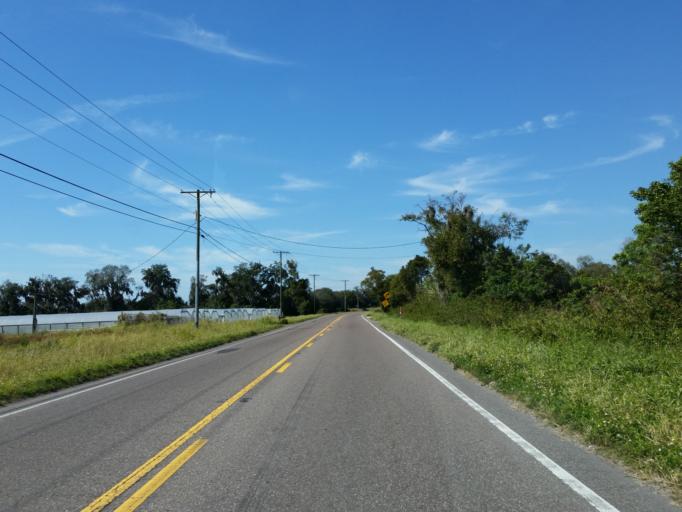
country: US
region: Florida
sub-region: Hillsborough County
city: Balm
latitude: 27.7629
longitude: -82.2630
